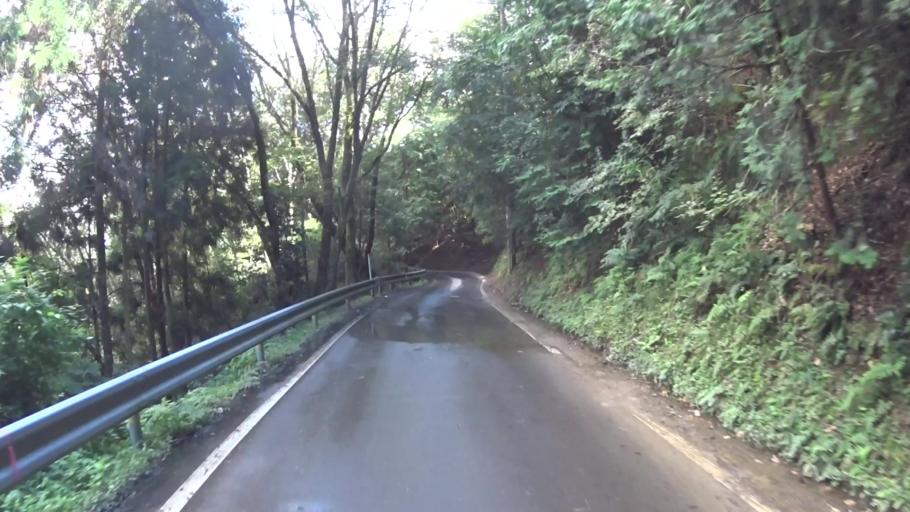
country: JP
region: Kyoto
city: Uji
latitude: 34.9145
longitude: 135.8505
